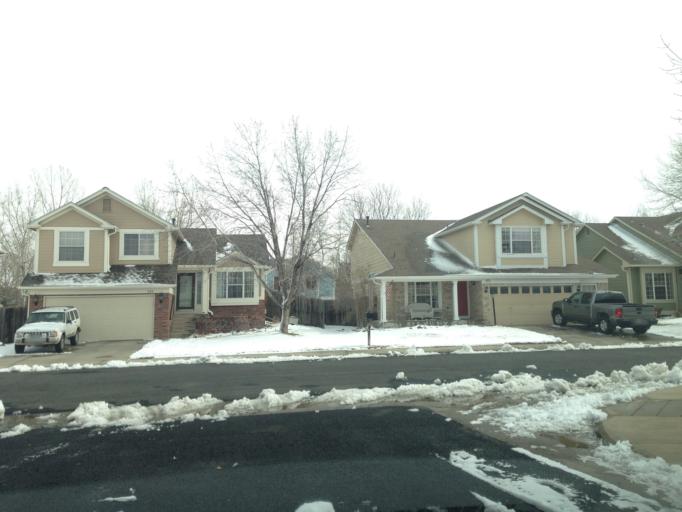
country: US
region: Colorado
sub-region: Boulder County
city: Lafayette
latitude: 39.9747
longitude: -105.0969
